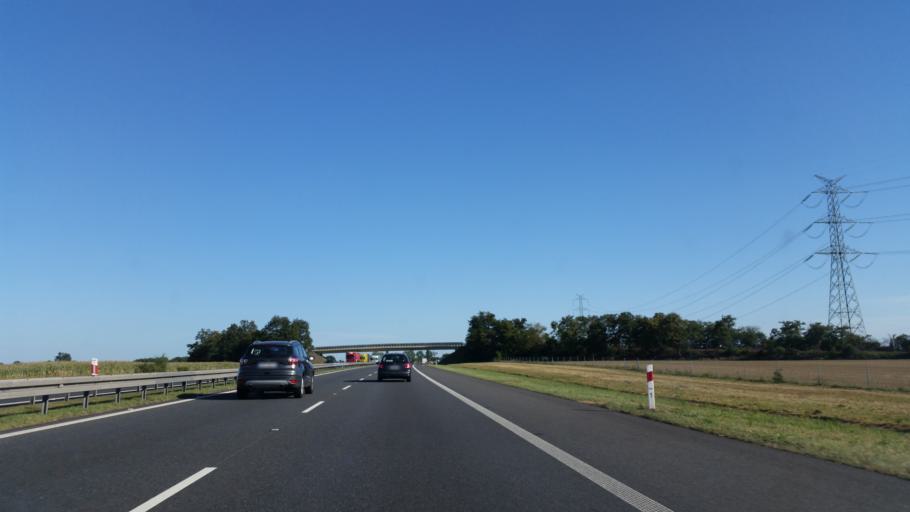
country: PL
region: Lower Silesian Voivodeship
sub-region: Powiat strzelinski
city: Wiazow
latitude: 50.8173
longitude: 17.3067
